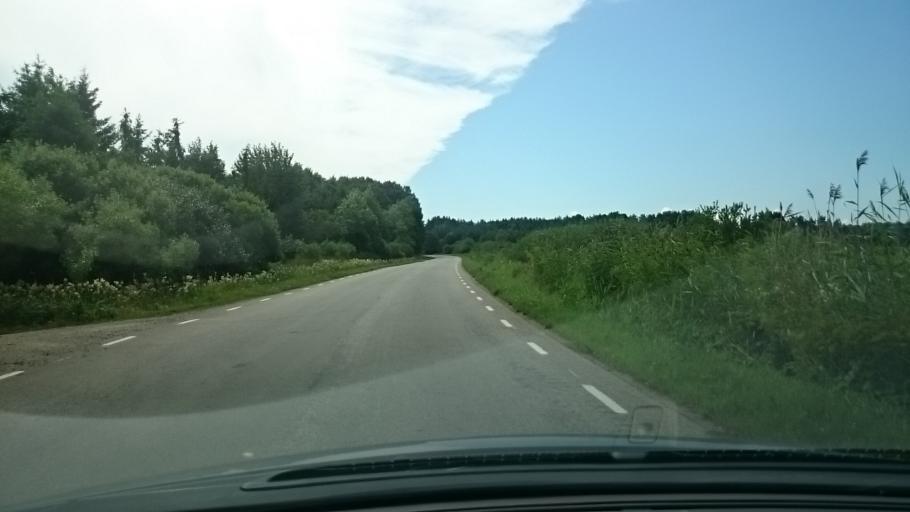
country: EE
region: Laeaene
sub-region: Haapsalu linn
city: Haapsalu
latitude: 59.0320
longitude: 23.5143
